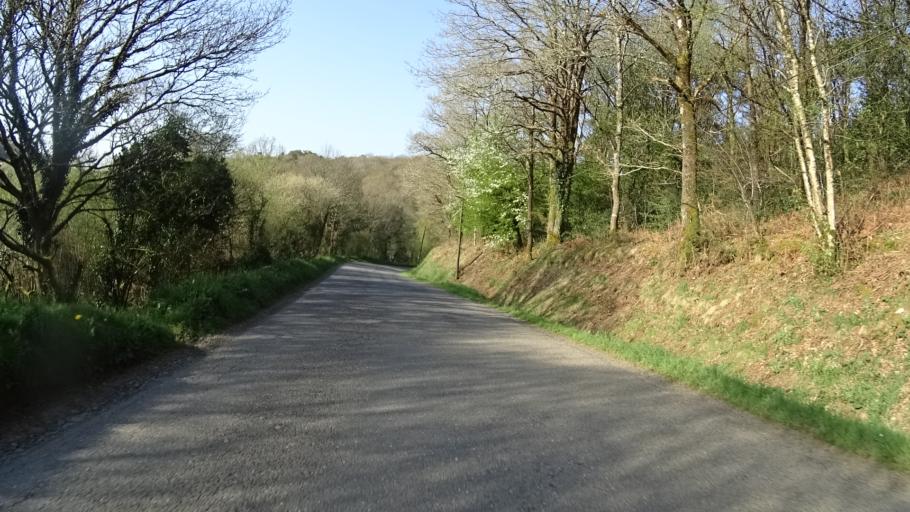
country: FR
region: Brittany
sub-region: Departement du Finistere
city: Sizun
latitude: 48.3877
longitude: -4.1374
